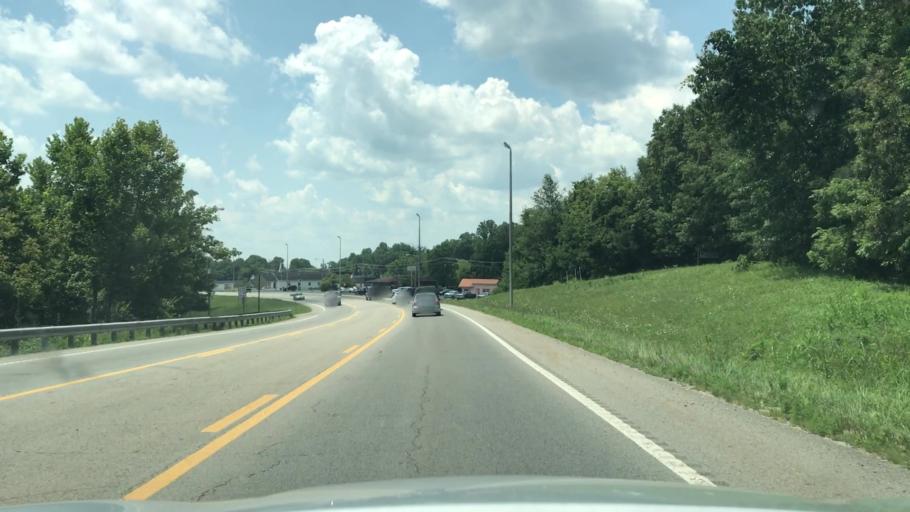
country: US
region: Tennessee
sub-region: Overton County
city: Livingston
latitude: 36.3904
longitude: -85.3338
